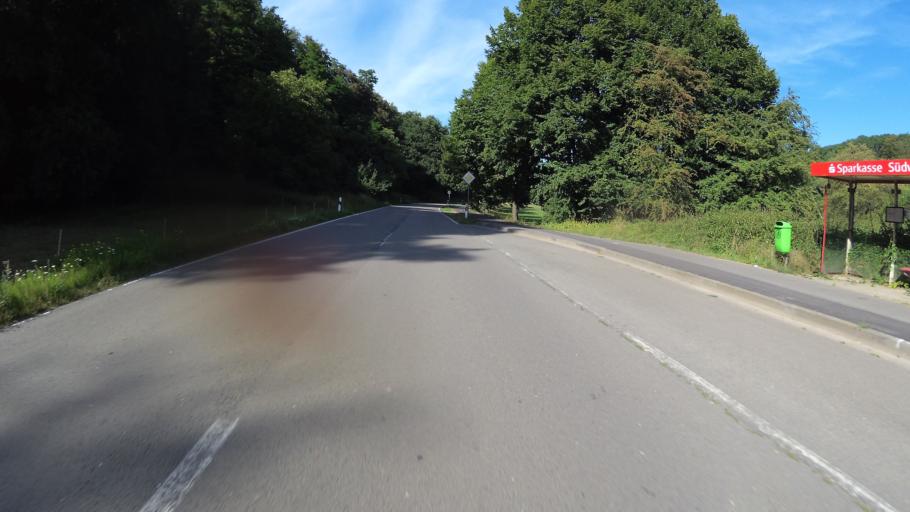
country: DE
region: Rheinland-Pfalz
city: Althornbach
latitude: 49.2209
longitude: 7.3509
